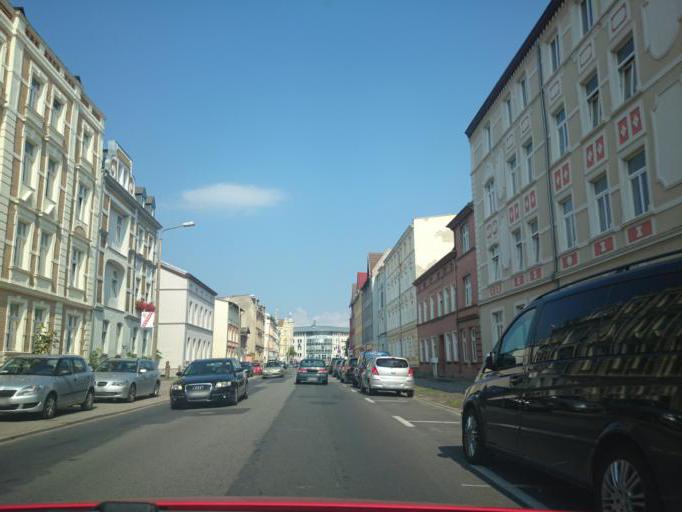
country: DE
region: Mecklenburg-Vorpommern
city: Stralsund
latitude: 54.3083
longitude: 13.0747
